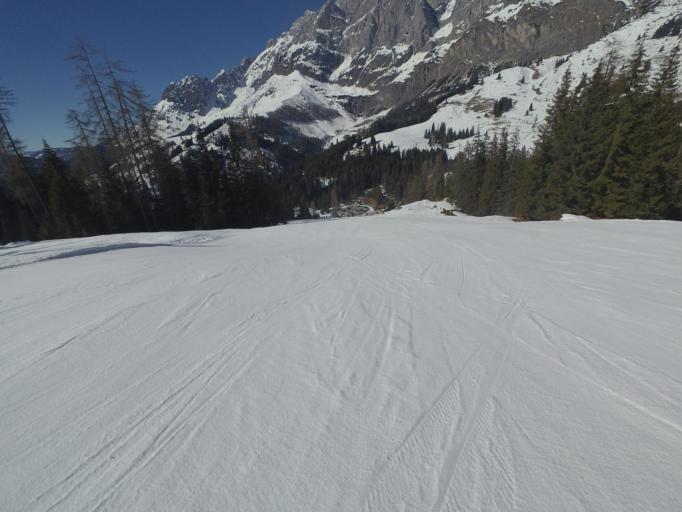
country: AT
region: Salzburg
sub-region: Politischer Bezirk Sankt Johann im Pongau
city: Muhlbach am Hochkonig
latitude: 47.3979
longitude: 13.1201
